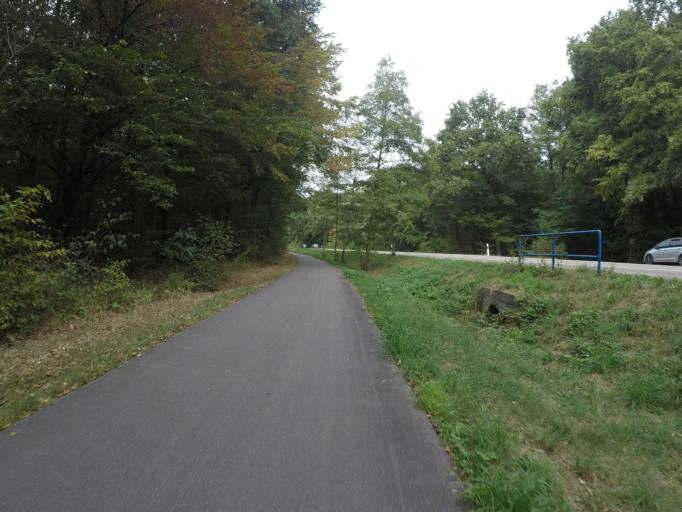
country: DE
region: Rheinland-Pfalz
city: Hanhofen
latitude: 49.3507
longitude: 8.3525
